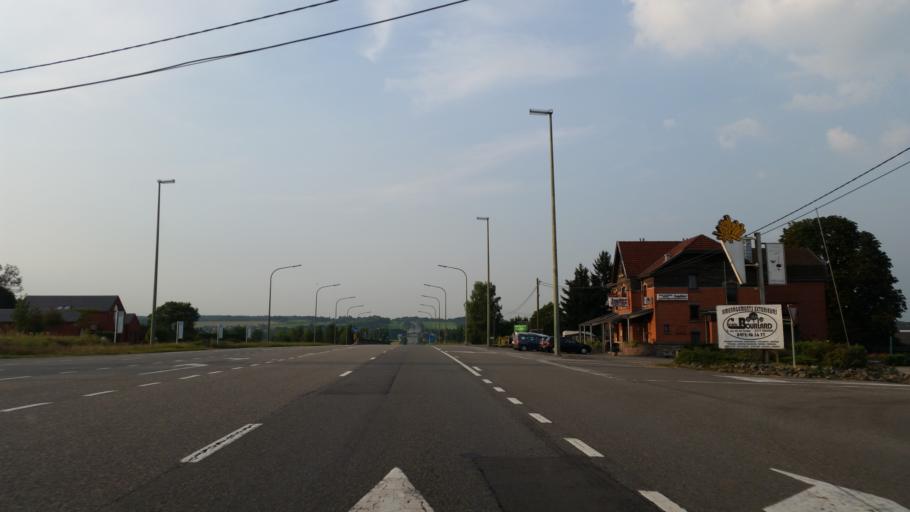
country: BE
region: Wallonia
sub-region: Province du Luxembourg
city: Marche-en-Famenne
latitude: 50.2773
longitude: 5.3481
